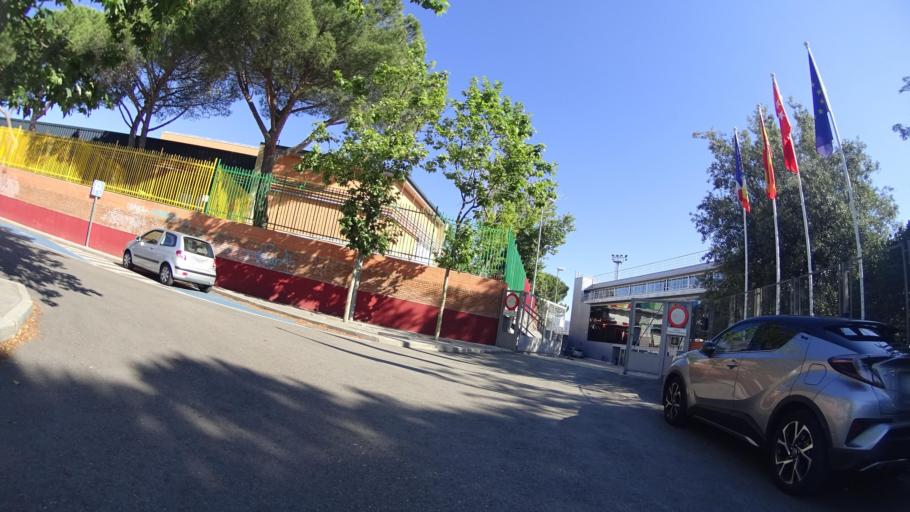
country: ES
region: Madrid
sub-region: Provincia de Madrid
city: Las Matas
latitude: 40.5540
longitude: -3.8863
